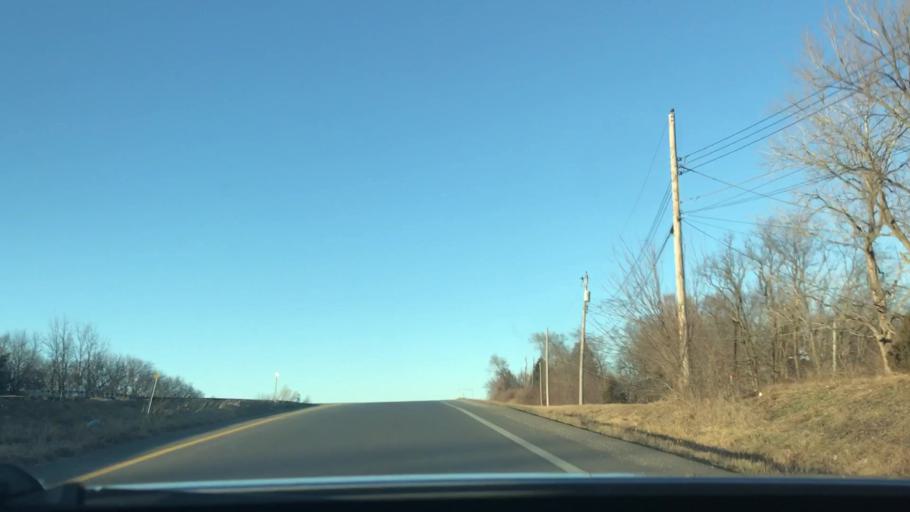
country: US
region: Missouri
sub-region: Clay County
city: Gladstone
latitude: 39.2203
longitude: -94.5891
